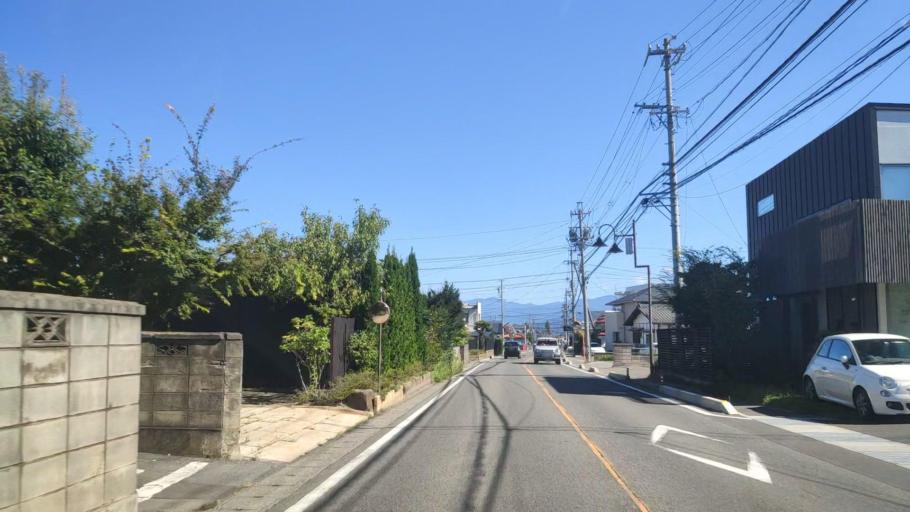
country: JP
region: Nagano
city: Shiojiri
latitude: 36.1461
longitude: 137.9440
